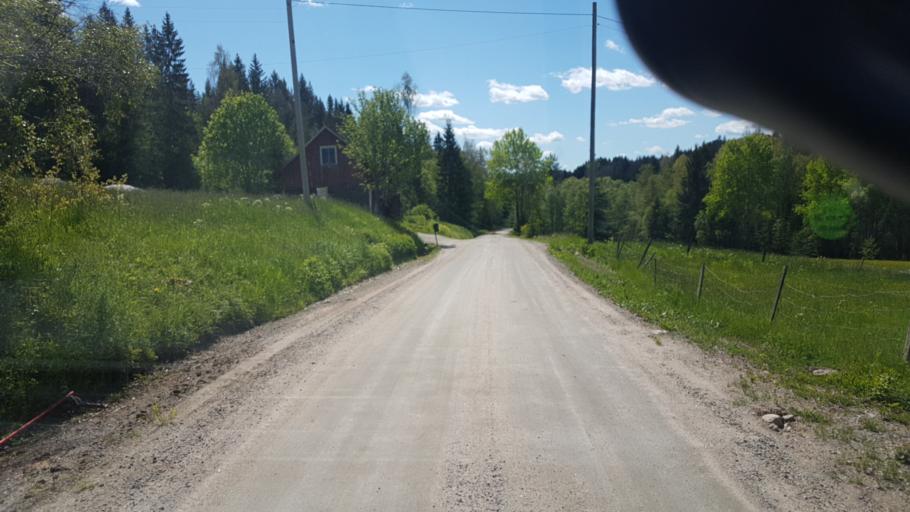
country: SE
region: Vaermland
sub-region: Arvika Kommun
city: Arvika
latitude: 59.6869
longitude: 12.7734
